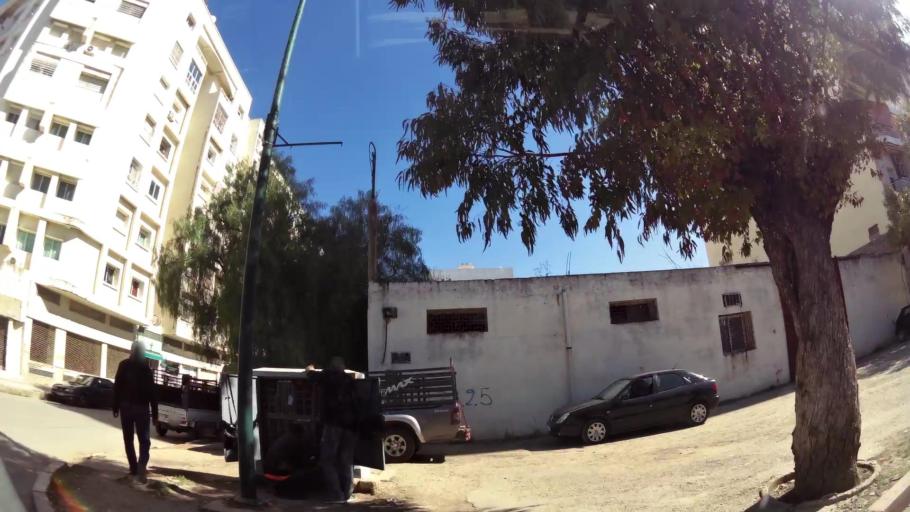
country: MA
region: Meknes-Tafilalet
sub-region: Meknes
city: Meknes
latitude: 33.8949
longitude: -5.5365
